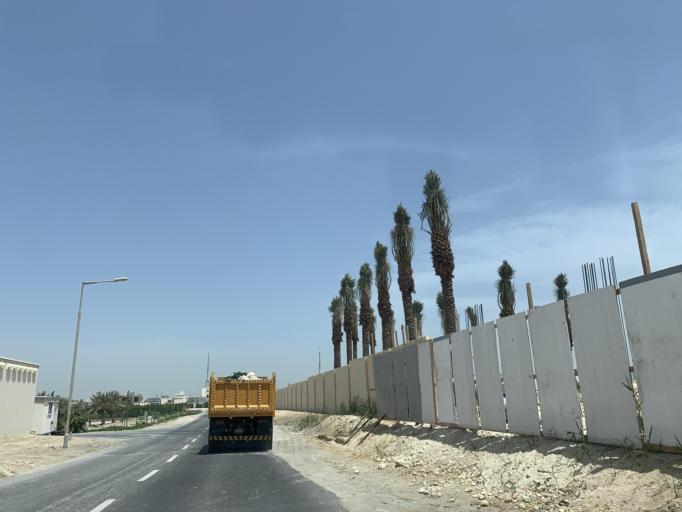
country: BH
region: Northern
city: Ar Rifa'
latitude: 26.1473
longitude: 50.5545
